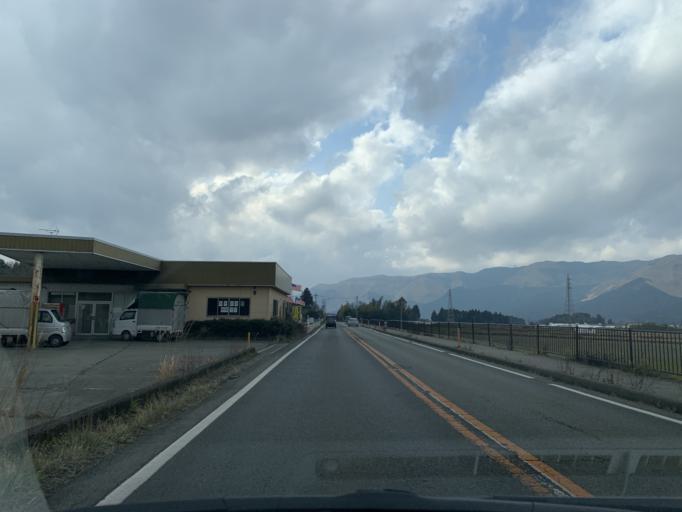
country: JP
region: Kumamoto
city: Aso
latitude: 32.9307
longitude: 131.0239
